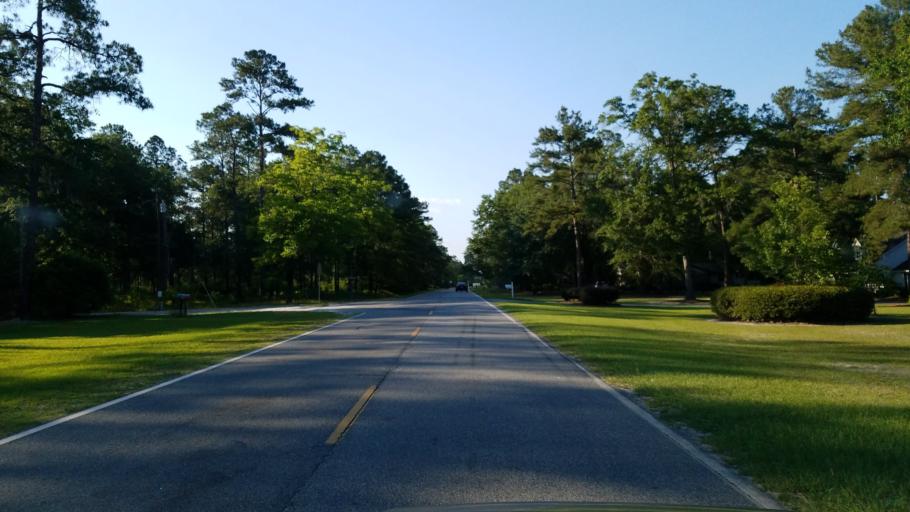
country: US
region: Georgia
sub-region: Lanier County
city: Lakeland
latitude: 30.9448
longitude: -83.0816
